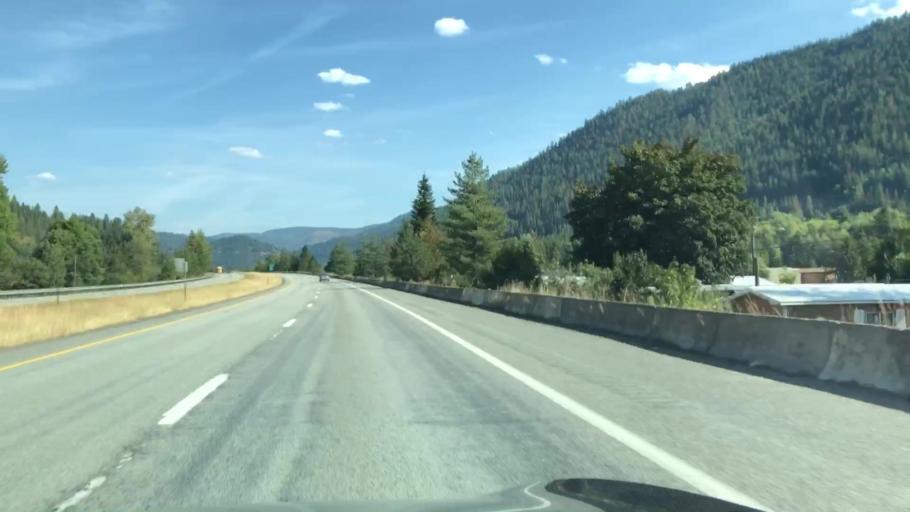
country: US
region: Idaho
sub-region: Shoshone County
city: Osburn
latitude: 47.5155
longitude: -116.0311
